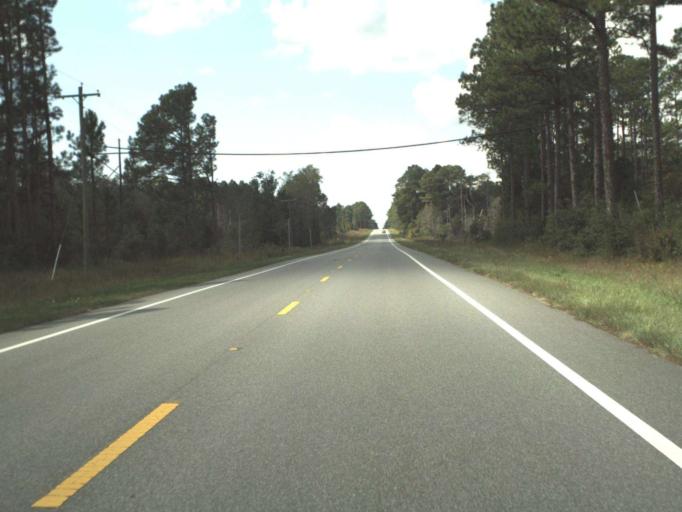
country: US
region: Florida
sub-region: Walton County
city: Freeport
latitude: 30.4756
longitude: -86.0148
